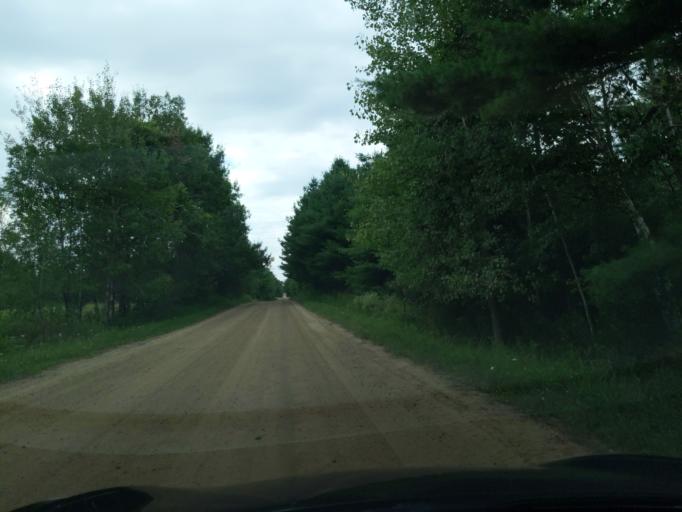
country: US
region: Michigan
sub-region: Clare County
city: Harrison
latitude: 44.0023
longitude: -85.0065
